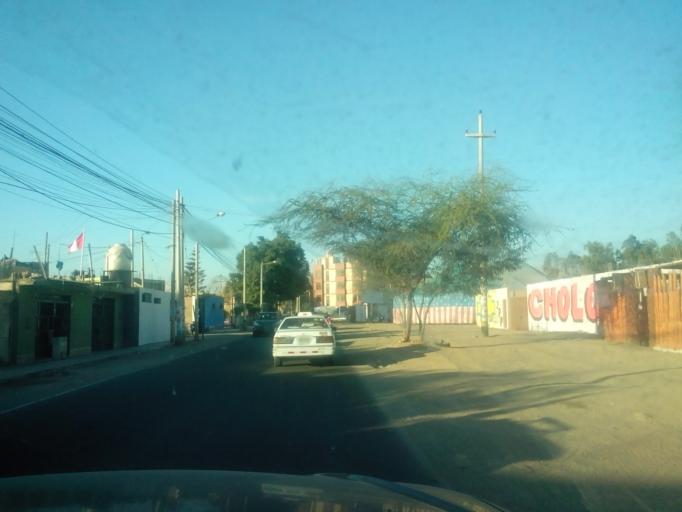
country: PE
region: Ica
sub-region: Provincia de Ica
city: Ica
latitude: -14.0779
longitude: -75.7447
